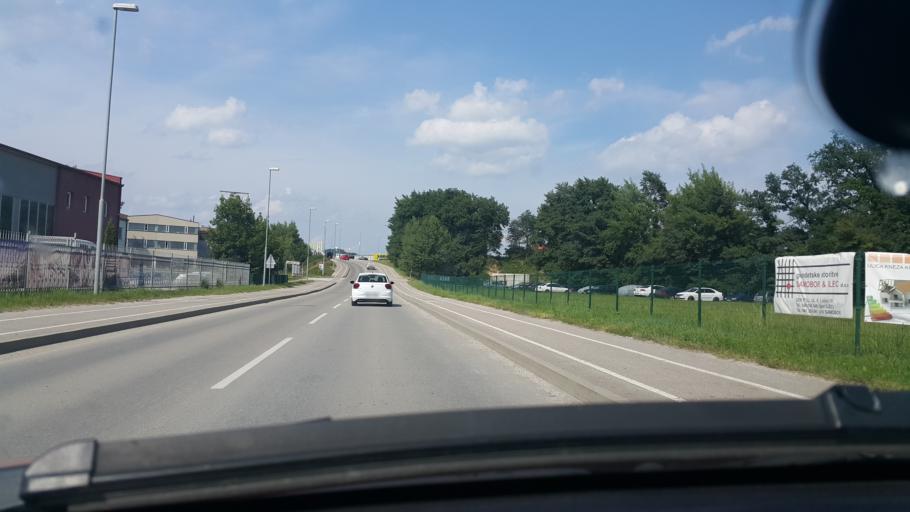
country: SI
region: Ptuj
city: Ptuj
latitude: 46.4242
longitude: 15.8903
